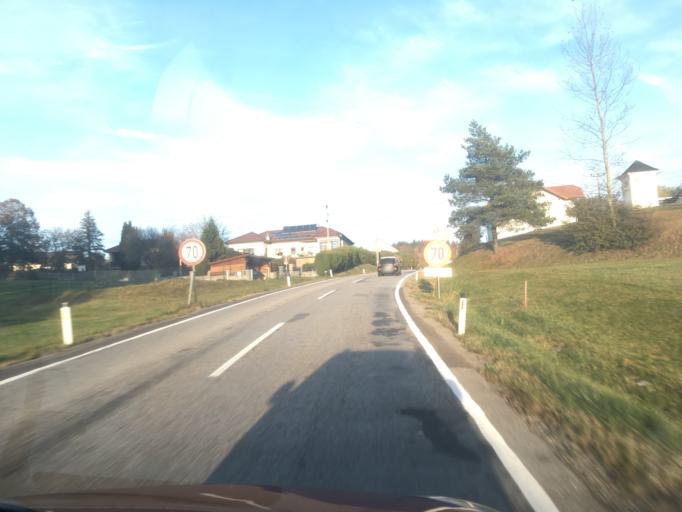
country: AT
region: Upper Austria
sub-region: Politischer Bezirk Freistadt
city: Freistadt
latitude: 48.5267
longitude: 14.5698
